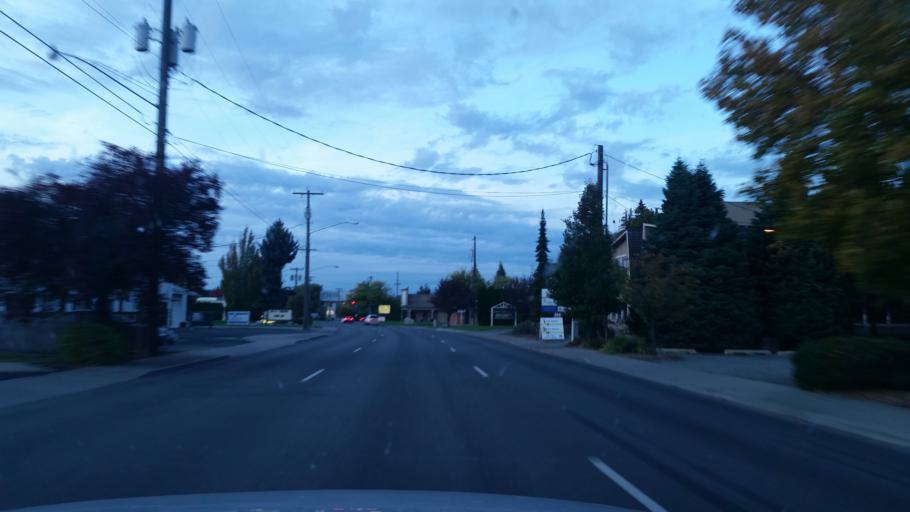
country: US
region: Washington
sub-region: Spokane County
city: Dishman
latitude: 47.6620
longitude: -117.2815
